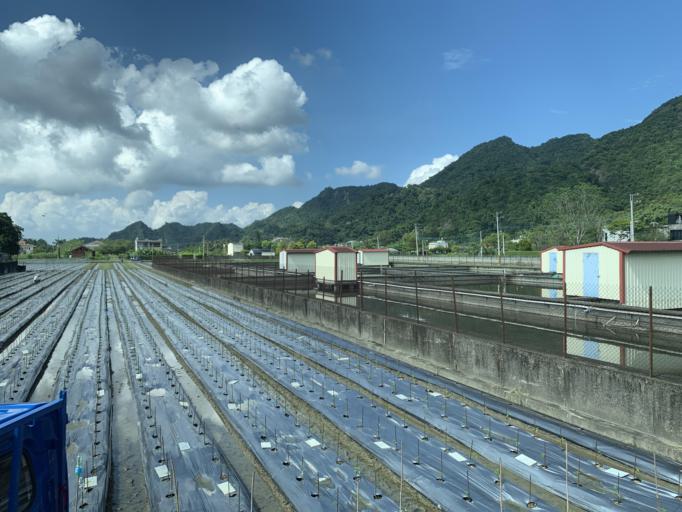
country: TW
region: Taiwan
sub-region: Pingtung
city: Pingtung
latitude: 22.8990
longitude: 120.5177
